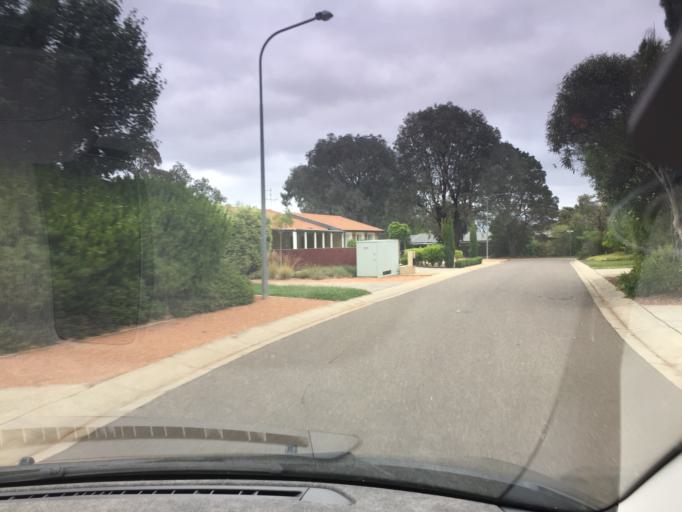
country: AU
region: Australian Capital Territory
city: Kaleen
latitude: -35.2184
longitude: 149.1147
